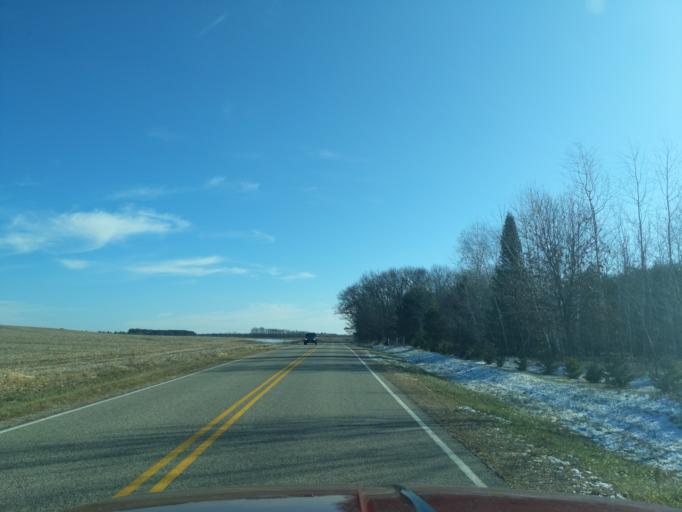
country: US
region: Wisconsin
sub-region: Waushara County
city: Silver Lake
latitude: 44.0926
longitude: -89.1836
